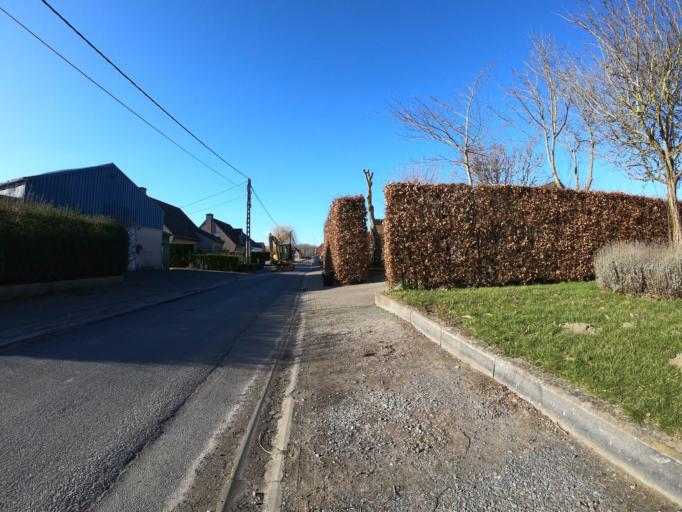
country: BE
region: Flanders
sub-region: Provincie West-Vlaanderen
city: Avelgem
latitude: 50.7857
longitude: 3.4598
